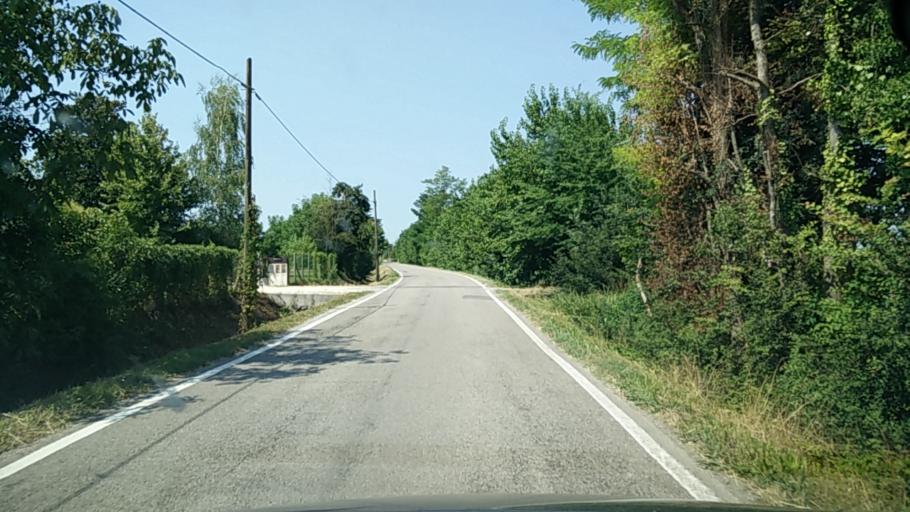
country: IT
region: Veneto
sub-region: Provincia di Treviso
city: Piavon
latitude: 45.7763
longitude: 12.5179
